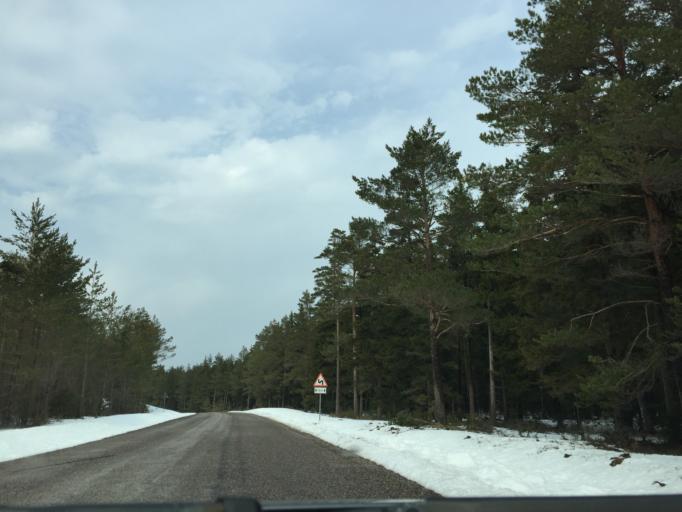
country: EE
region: Saare
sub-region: Kuressaare linn
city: Kuressaare
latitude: 58.3957
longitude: 22.1742
